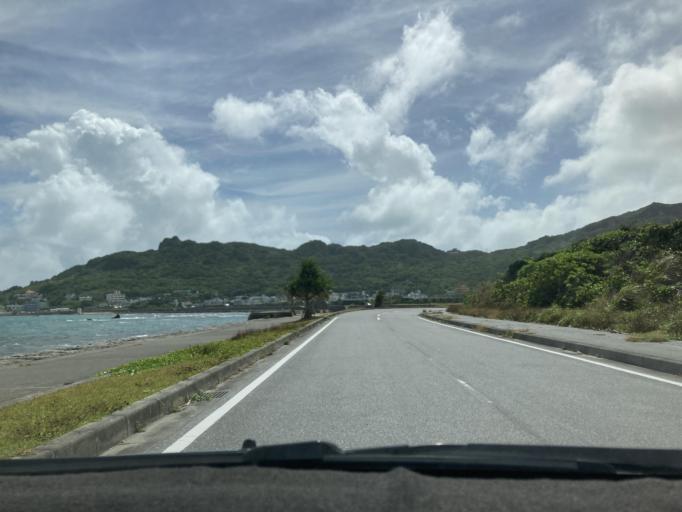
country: JP
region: Okinawa
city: Ginowan
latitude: 26.1846
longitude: 127.8217
